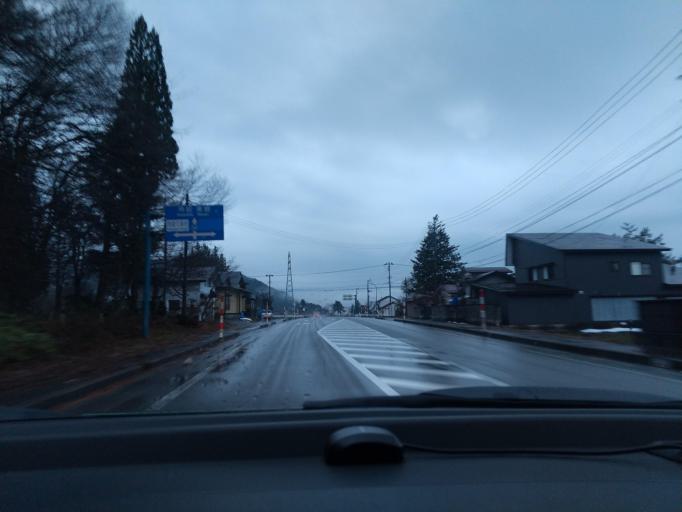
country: JP
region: Akita
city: Kakunodatemachi
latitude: 39.6163
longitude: 140.6311
